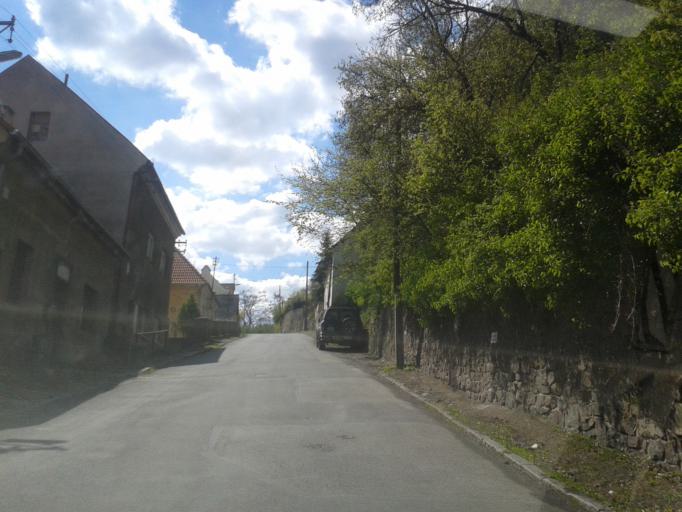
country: CZ
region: Central Bohemia
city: Nizbor
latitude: 49.9992
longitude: 14.0007
